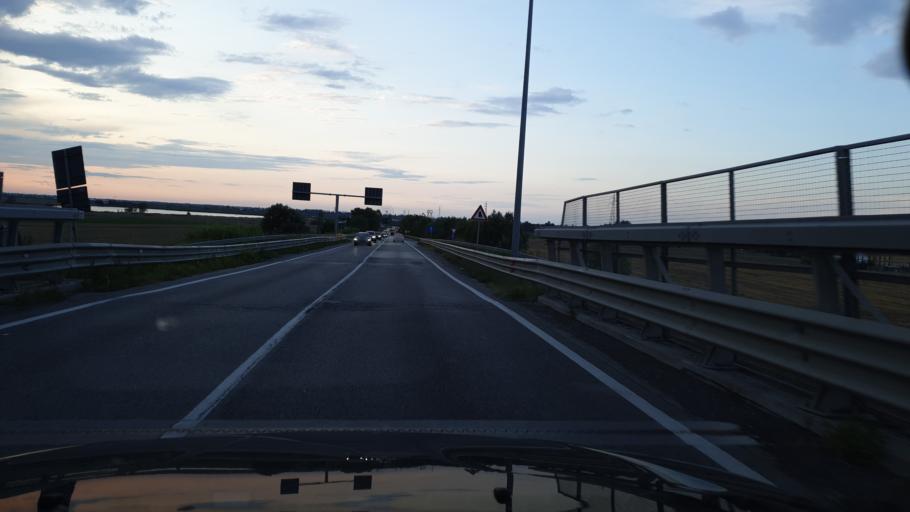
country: IT
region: Emilia-Romagna
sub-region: Provincia di Ravenna
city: Savio
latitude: 44.3042
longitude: 12.2894
